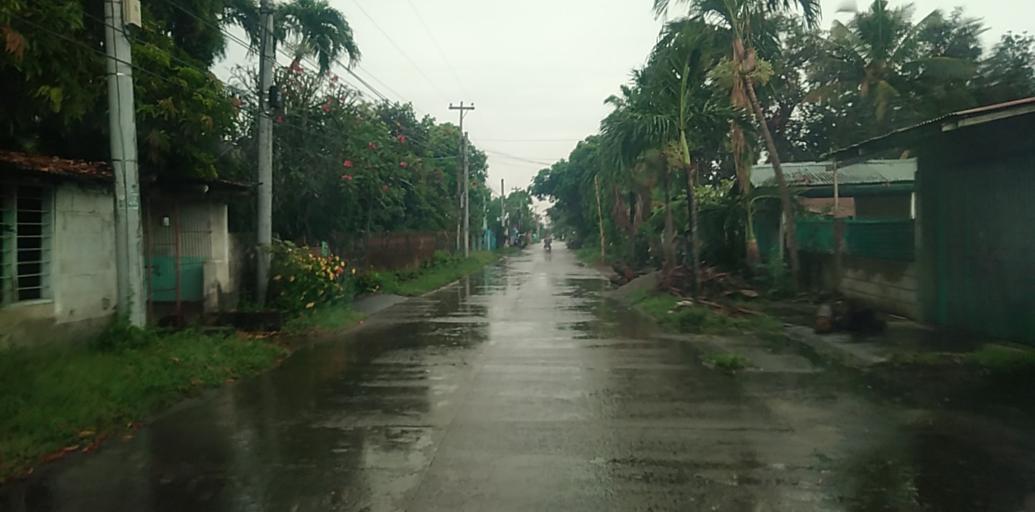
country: PH
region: Central Luzon
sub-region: Province of Pampanga
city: Arenas
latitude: 15.1685
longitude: 120.6867
